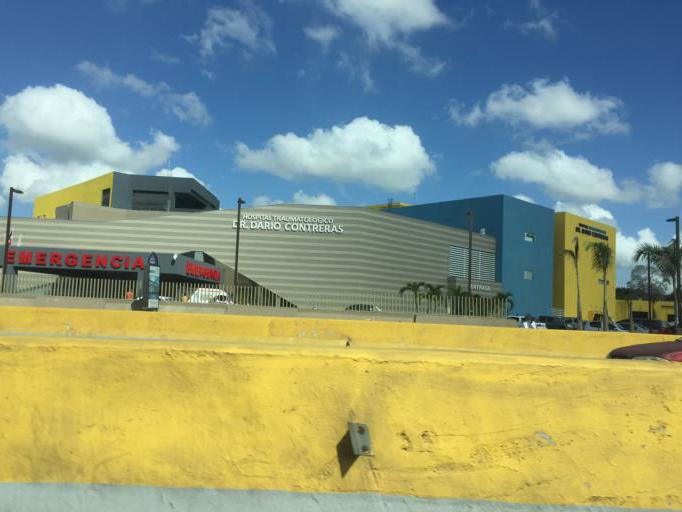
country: DO
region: Santo Domingo
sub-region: Santo Domingo
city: Santo Domingo Este
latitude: 18.4848
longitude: -69.8631
